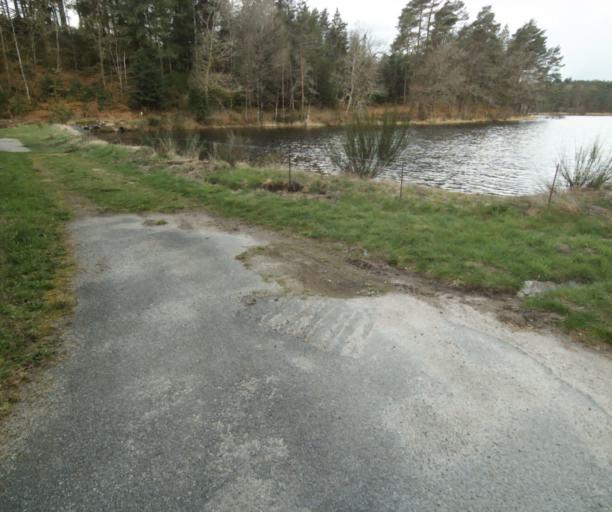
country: FR
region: Limousin
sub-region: Departement de la Correze
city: Correze
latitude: 45.2696
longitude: 1.9465
